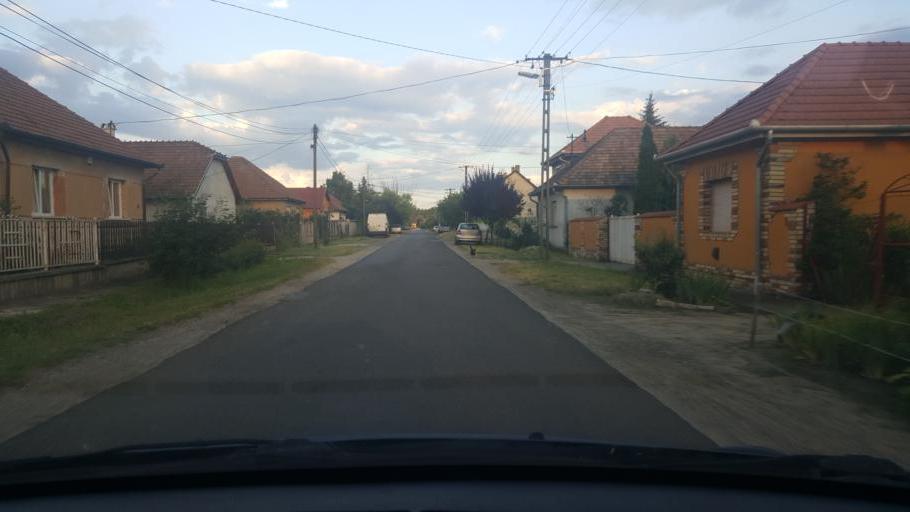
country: HU
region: Pest
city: Monor
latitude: 47.3358
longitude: 19.4423
